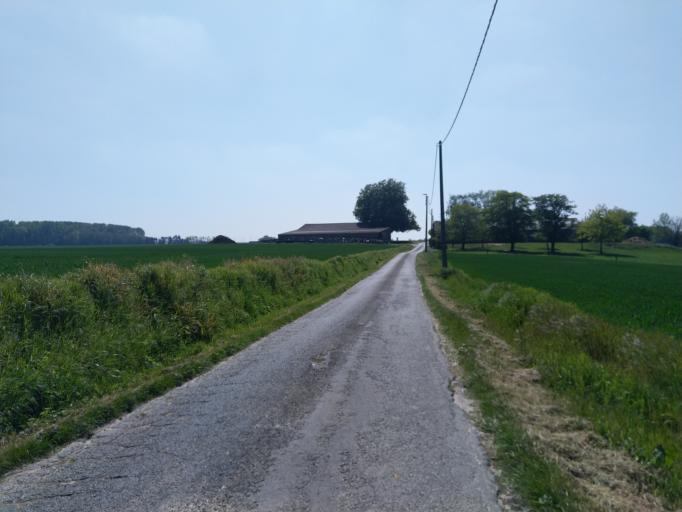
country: BE
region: Wallonia
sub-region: Province du Hainaut
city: Soignies
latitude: 50.6004
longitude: 4.0979
